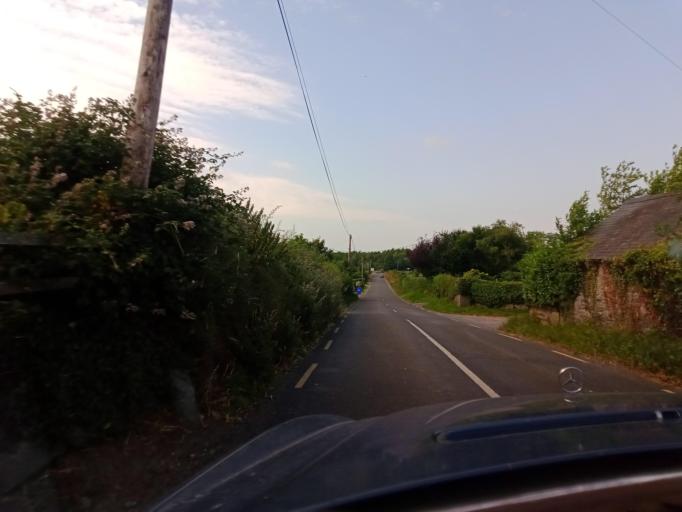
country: IE
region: Leinster
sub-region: Kilkenny
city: Callan
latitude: 52.4869
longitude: -7.3233
